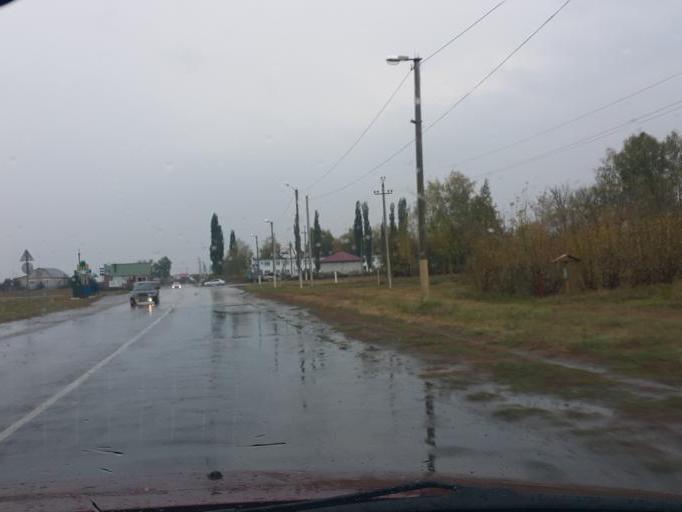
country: RU
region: Tambov
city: Znamenka
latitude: 52.4059
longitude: 41.4621
